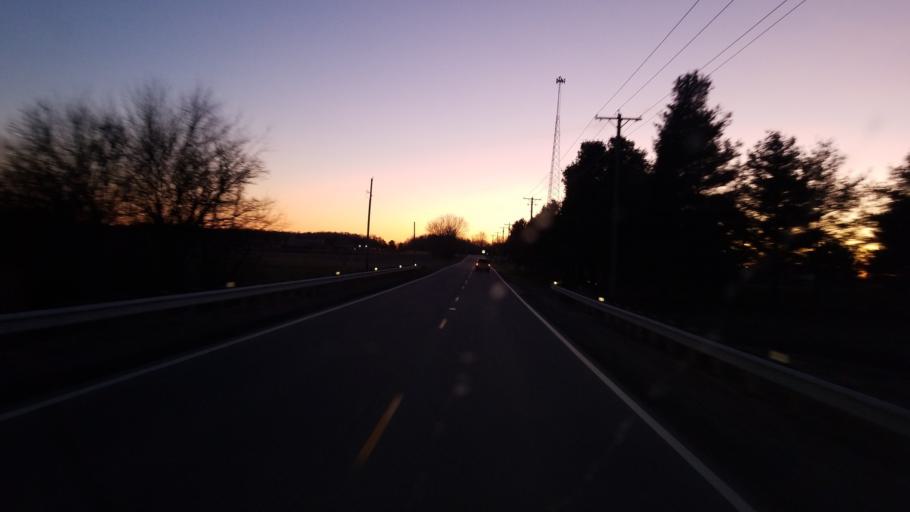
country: US
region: Ohio
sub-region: Highland County
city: Leesburg
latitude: 39.3809
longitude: -83.5431
